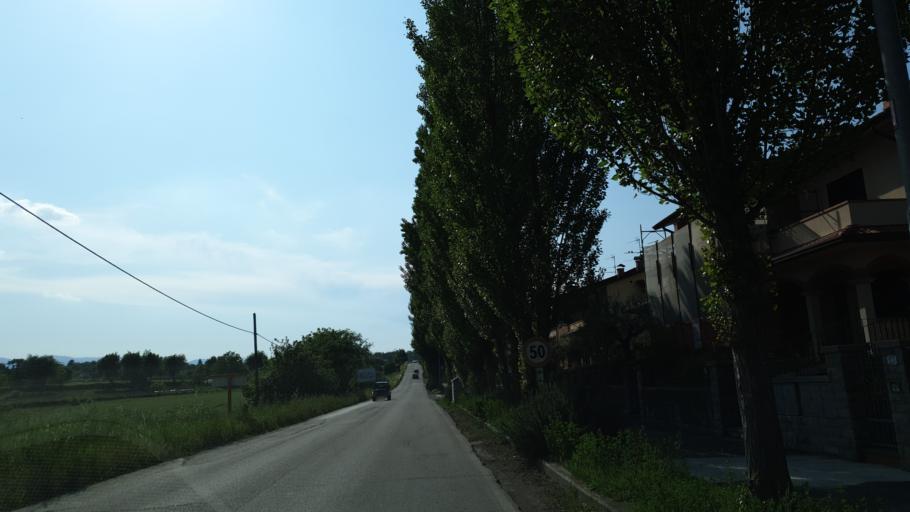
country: IT
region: Tuscany
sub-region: Province of Arezzo
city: Soci
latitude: 43.7372
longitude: 11.8087
